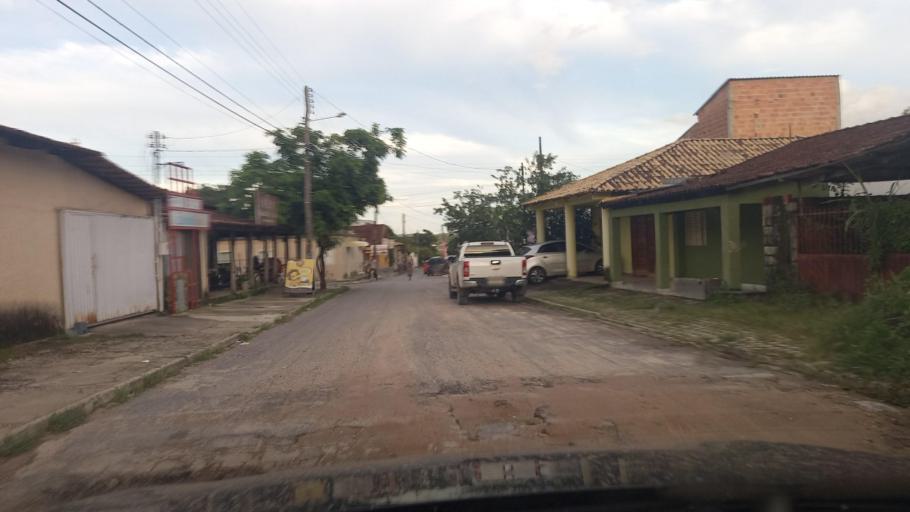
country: BR
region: Goias
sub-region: Cavalcante
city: Cavalcante
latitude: -13.7980
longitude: -47.4597
